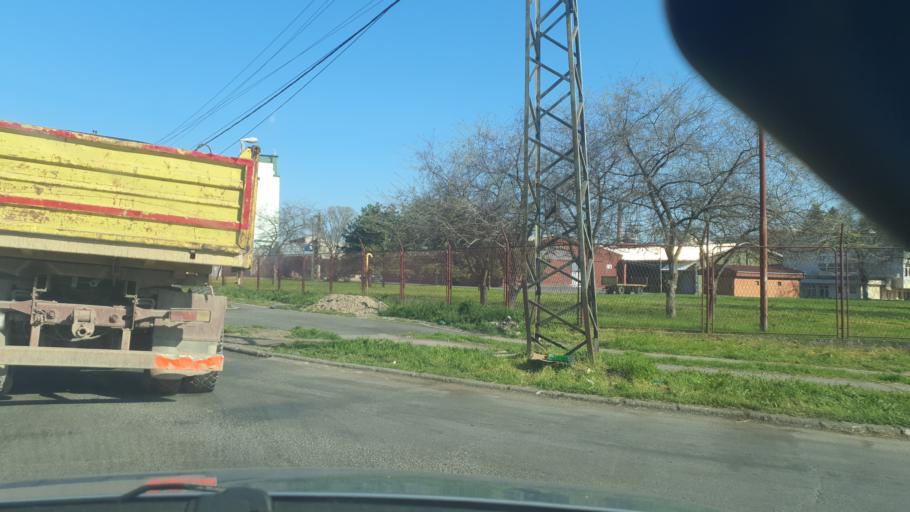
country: RS
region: Autonomna Pokrajina Vojvodina
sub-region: Juznobacki Okrug
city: Vrbas
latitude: 45.5775
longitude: 19.6277
